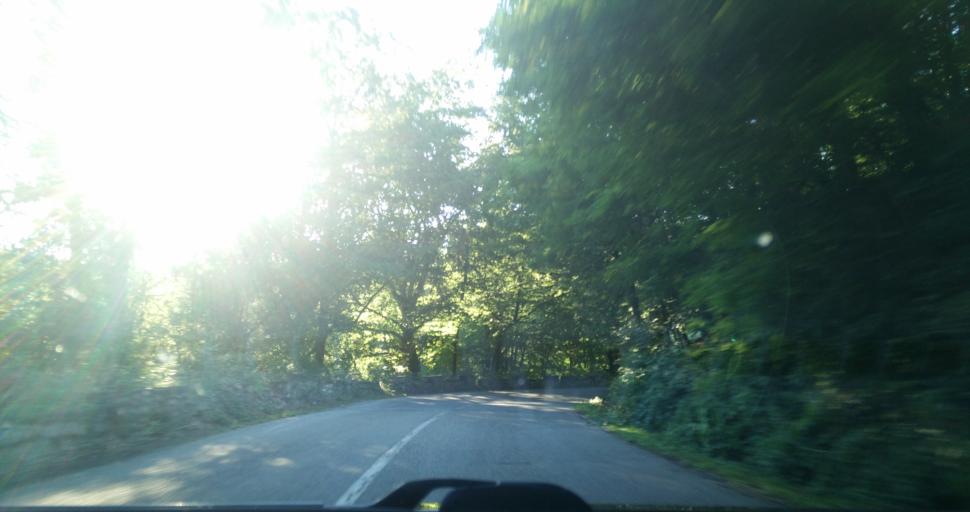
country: RO
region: Bihor
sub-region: Oras Nucet
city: Nucet
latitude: 46.4875
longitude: 22.6056
